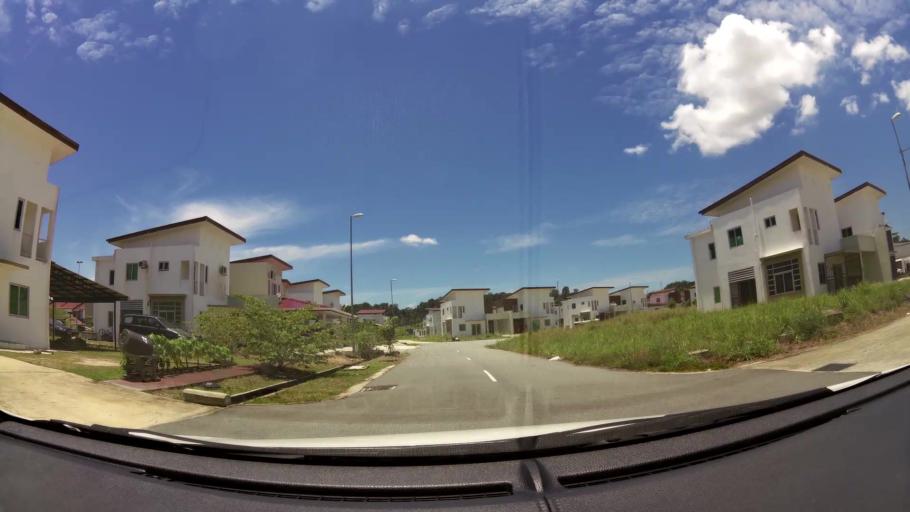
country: BN
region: Brunei and Muara
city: Bandar Seri Begawan
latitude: 5.0058
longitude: 115.0075
